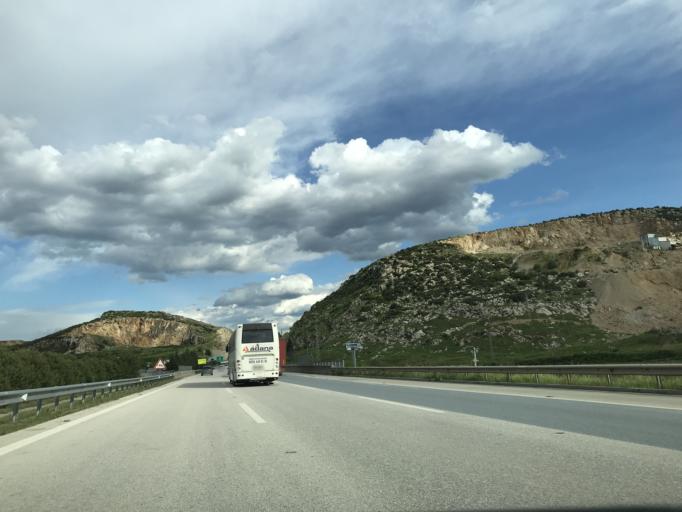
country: TR
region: Adana
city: Ceyhan
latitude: 37.0012
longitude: 35.7284
